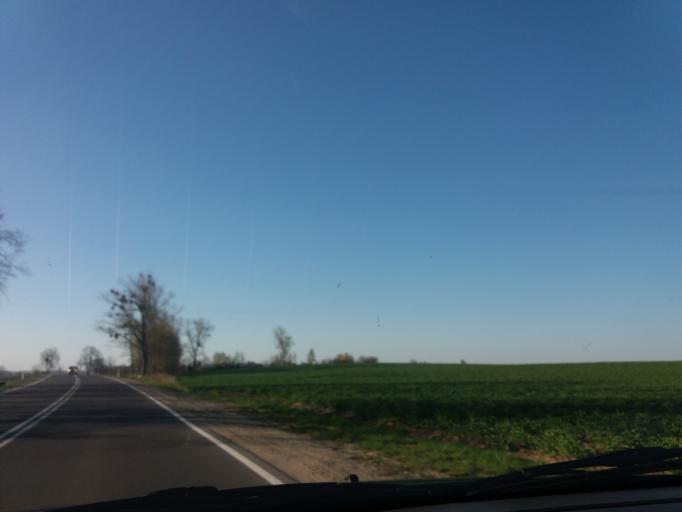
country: PL
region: Warmian-Masurian Voivodeship
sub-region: Powiat nidzicki
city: Nidzica
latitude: 53.3356
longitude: 20.4381
